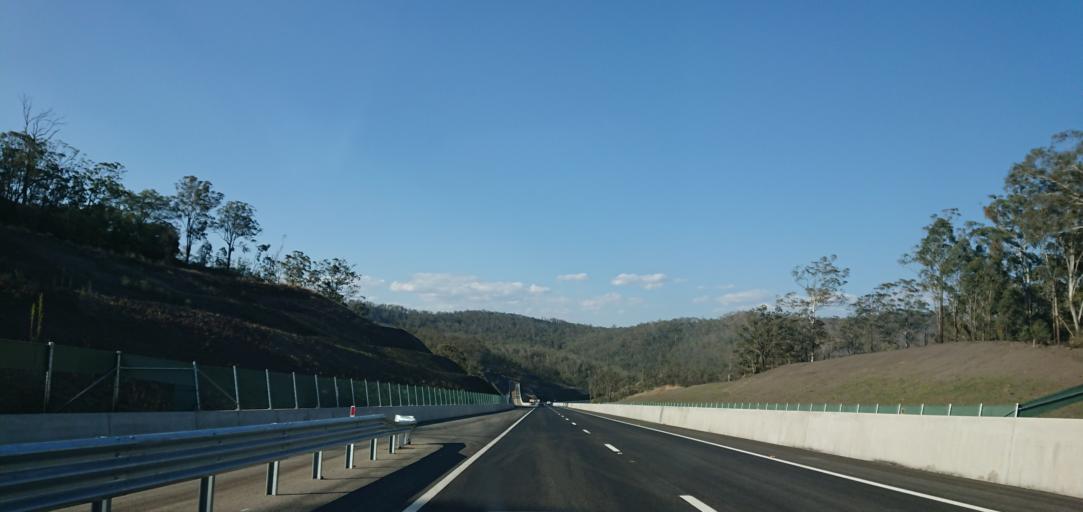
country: AU
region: Queensland
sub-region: Toowoomba
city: Wilsonton Heights
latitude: -27.5051
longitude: 151.9719
